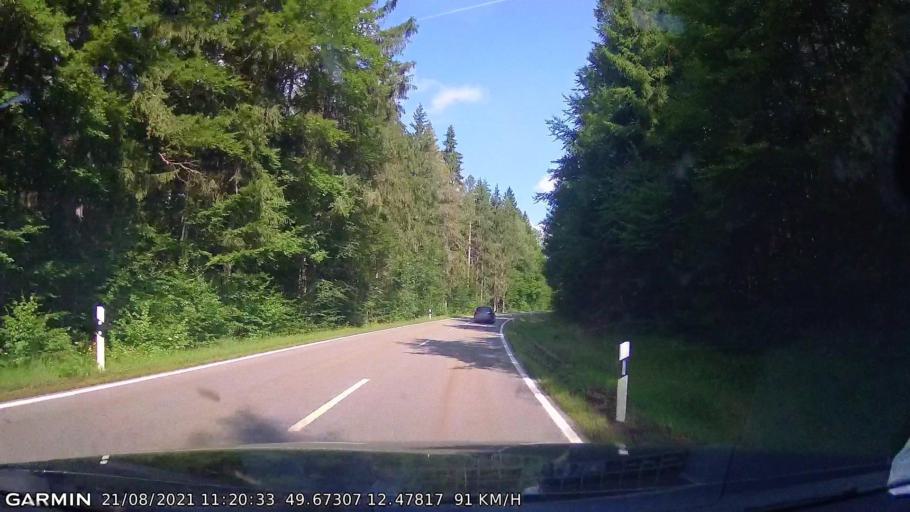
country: DE
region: Bavaria
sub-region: Upper Palatinate
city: Waidhaus
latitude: 49.6732
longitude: 12.4781
